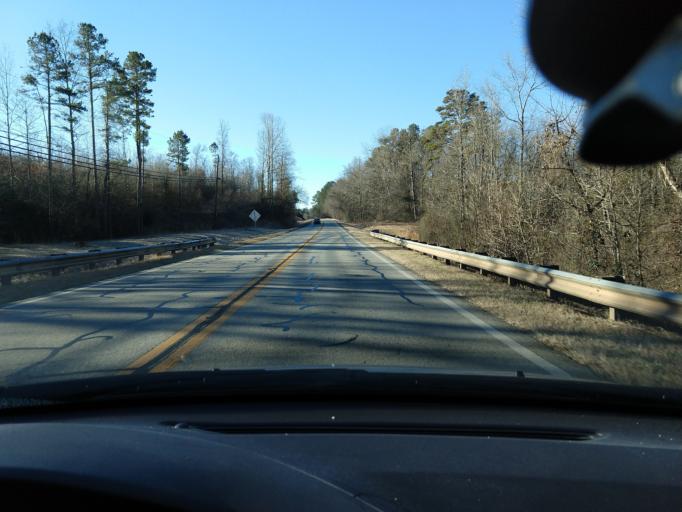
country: US
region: Georgia
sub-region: Jackson County
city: Commerce
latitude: 34.2236
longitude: -83.4568
